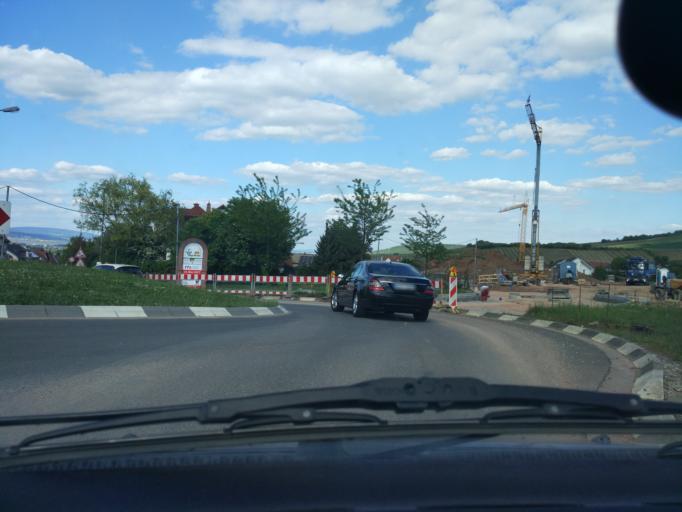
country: DE
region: Rheinland-Pfalz
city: Ockenheim
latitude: 49.9394
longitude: 7.9696
